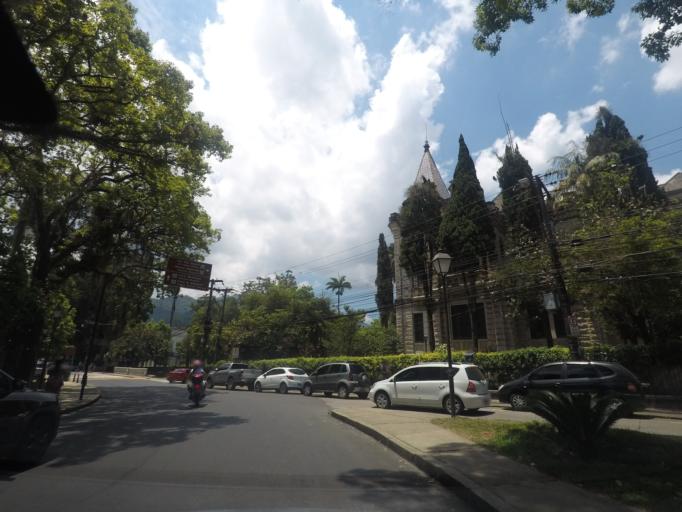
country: BR
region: Rio de Janeiro
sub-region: Petropolis
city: Petropolis
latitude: -22.5094
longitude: -43.1820
